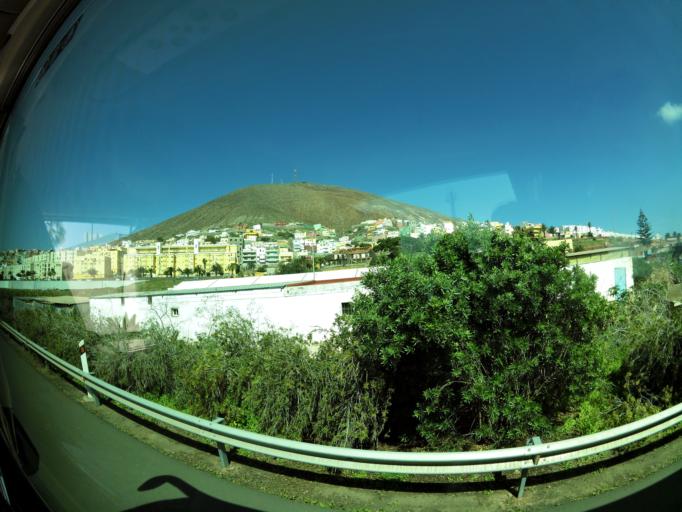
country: ES
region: Canary Islands
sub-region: Provincia de Las Palmas
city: Guia
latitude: 28.1435
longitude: -15.6405
